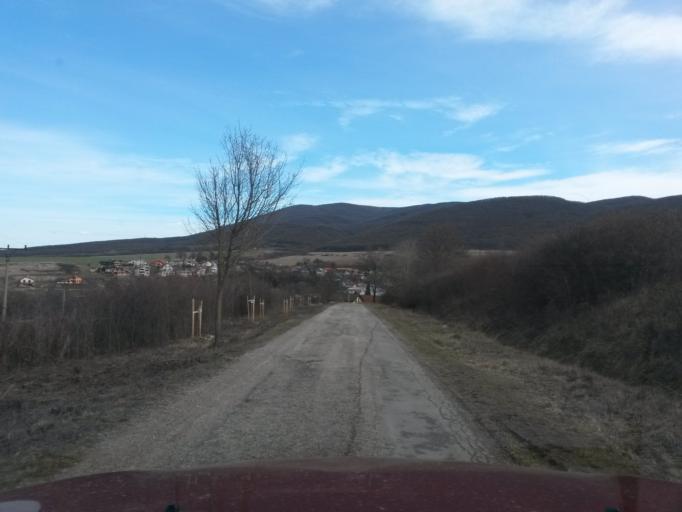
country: HU
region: Borsod-Abauj-Zemplen
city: Gonc
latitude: 48.5862
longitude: 21.3695
